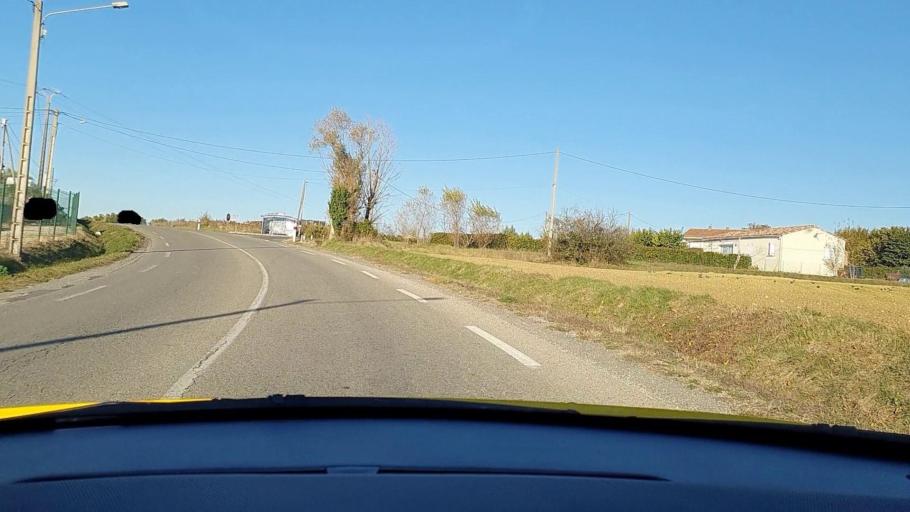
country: FR
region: Languedoc-Roussillon
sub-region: Departement du Gard
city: Salindres
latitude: 44.1780
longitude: 4.1646
